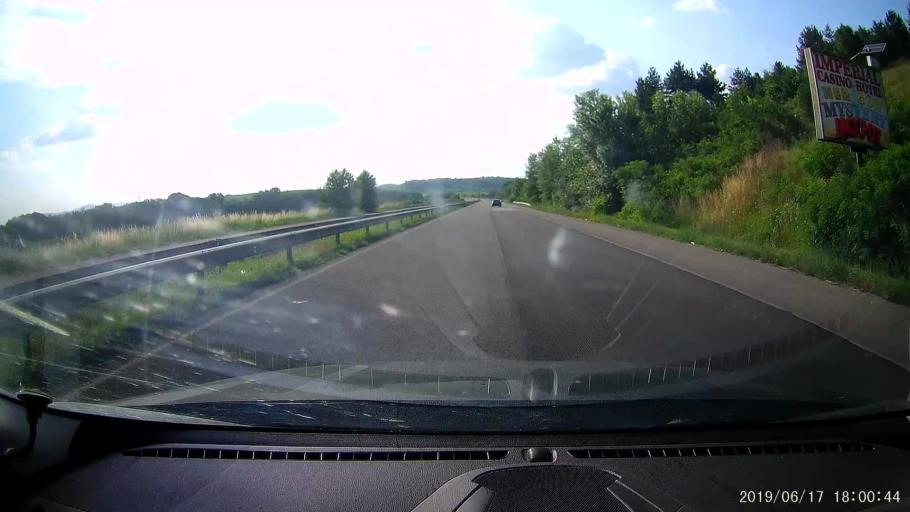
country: BG
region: Khaskovo
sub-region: Obshtina Svilengrad
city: Svilengrad
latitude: 41.7399
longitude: 26.2730
